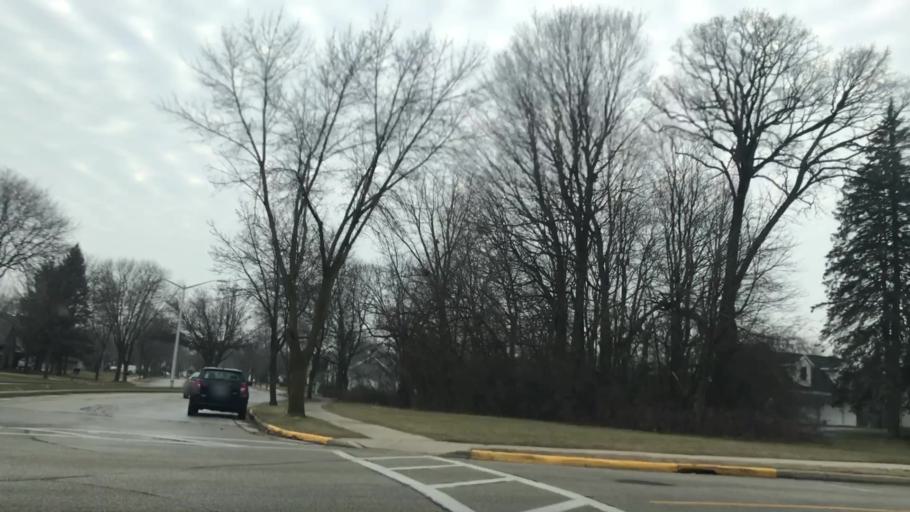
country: US
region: Wisconsin
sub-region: Ozaukee County
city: Cedarburg
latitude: 43.2938
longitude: -87.9950
